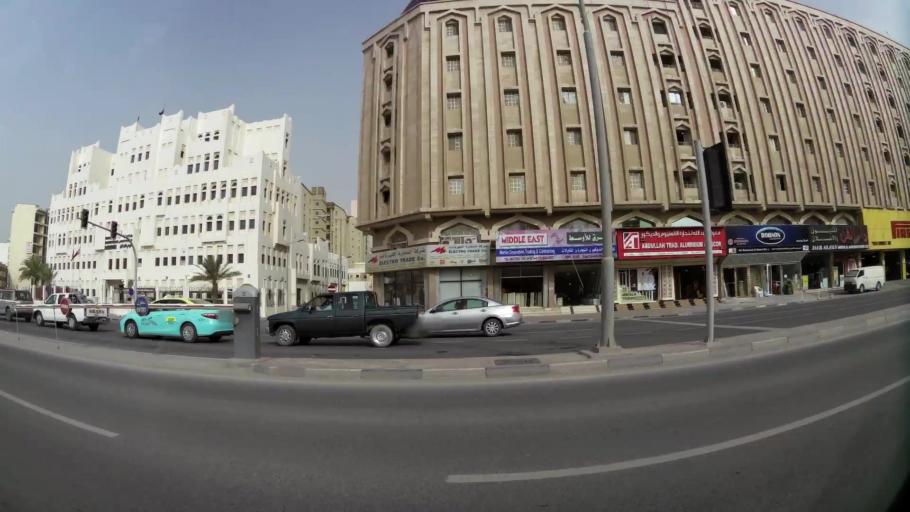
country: QA
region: Baladiyat ad Dawhah
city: Doha
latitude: 25.2769
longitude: 51.5402
